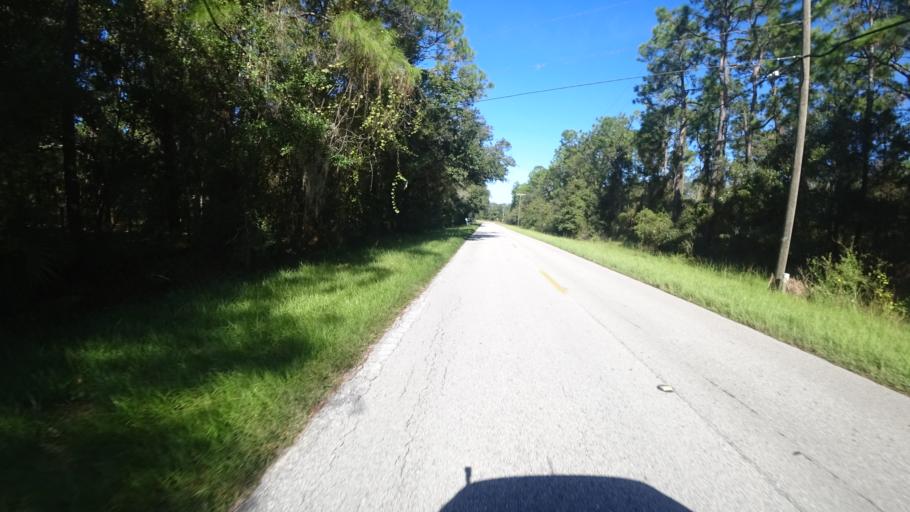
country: US
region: Florida
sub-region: Hillsborough County
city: Sun City Center
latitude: 27.6734
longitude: -82.3471
